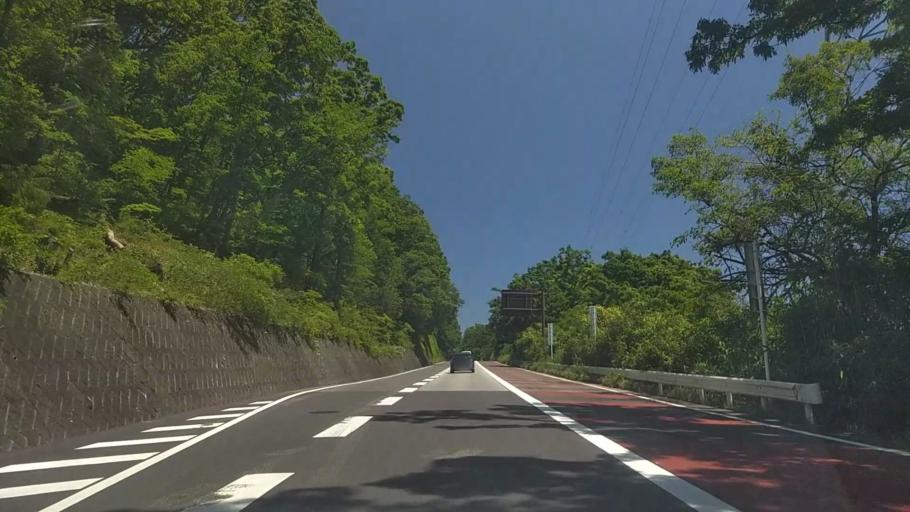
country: JP
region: Yamanashi
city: Nirasaki
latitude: 35.8018
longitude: 138.4257
